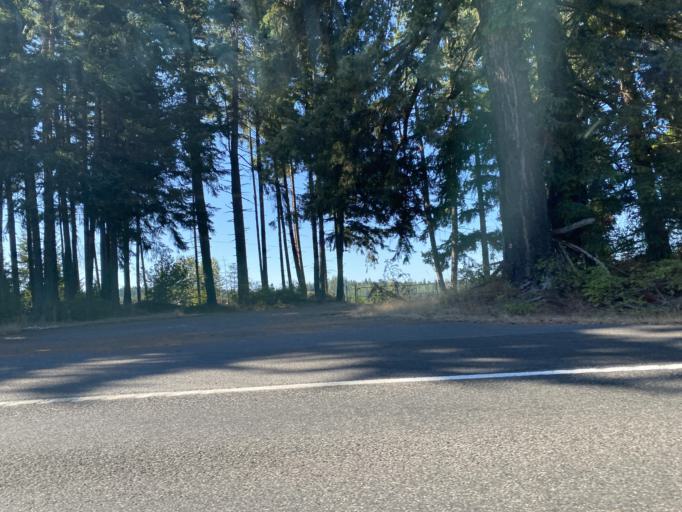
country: US
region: Washington
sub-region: Thurston County
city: Tanglewilde-Thompson Place
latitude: 46.9857
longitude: -122.7507
